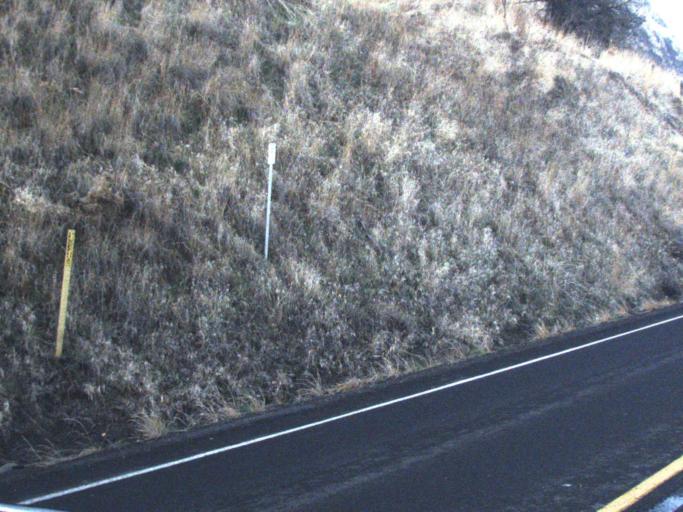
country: US
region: Washington
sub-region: Asotin County
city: Asotin
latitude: 46.3428
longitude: -117.0572
